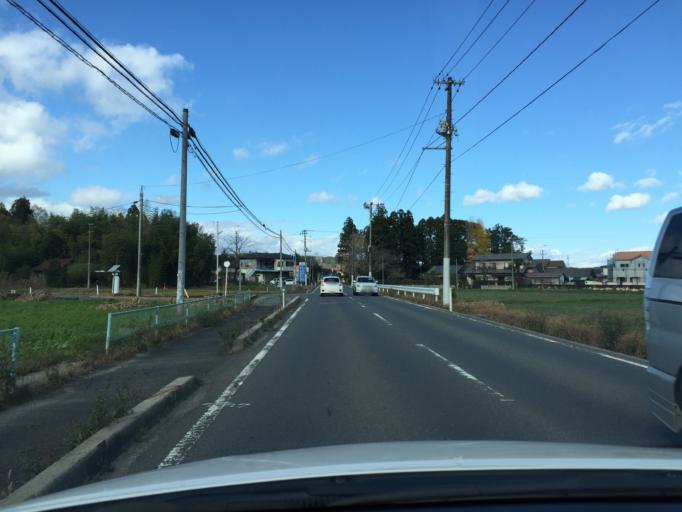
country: JP
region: Fukushima
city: Namie
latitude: 37.6530
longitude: 140.9436
